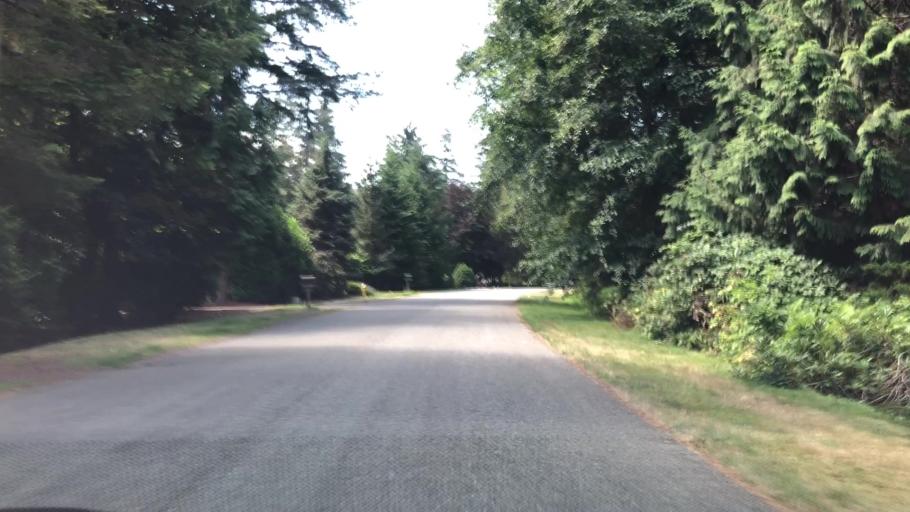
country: US
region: Washington
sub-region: King County
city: Cottage Lake
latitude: 47.7343
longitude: -122.0940
